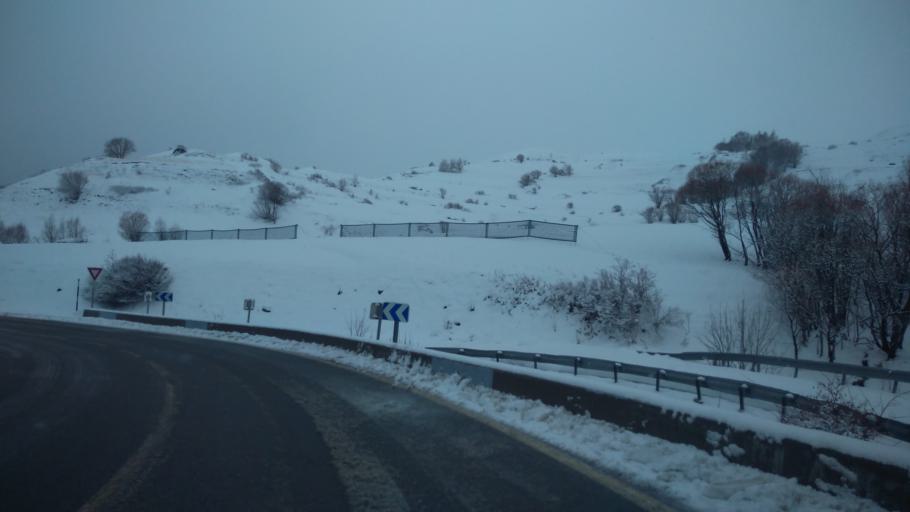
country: FR
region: Rhone-Alpes
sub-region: Departement de la Savoie
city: Valloire
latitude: 45.0425
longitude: 6.3555
